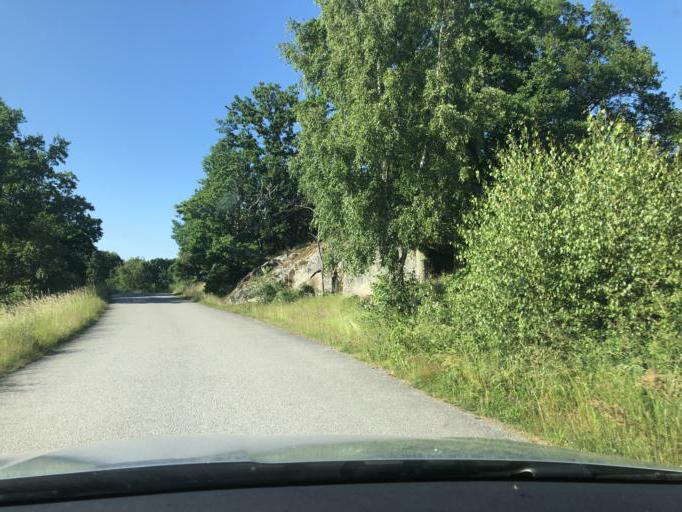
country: SE
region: Blekinge
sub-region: Karlshamns Kommun
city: Morrum
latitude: 56.1609
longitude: 14.8013
